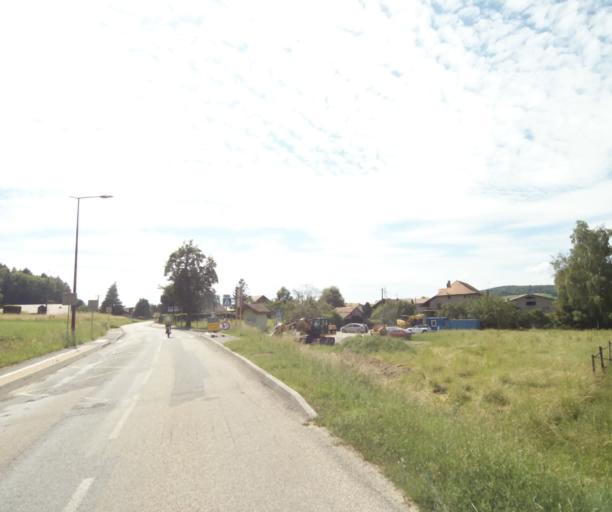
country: FR
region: Rhone-Alpes
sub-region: Departement de la Haute-Savoie
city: Perrignier
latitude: 46.3067
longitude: 6.4696
